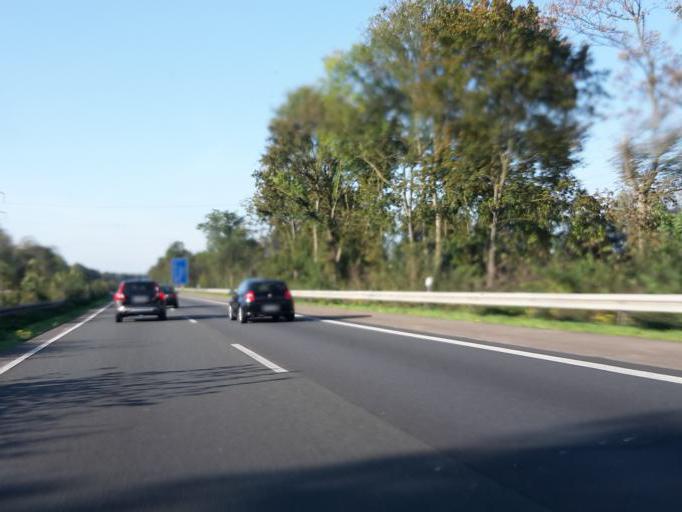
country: DE
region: North Rhine-Westphalia
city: Werne
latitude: 51.6885
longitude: 7.6730
